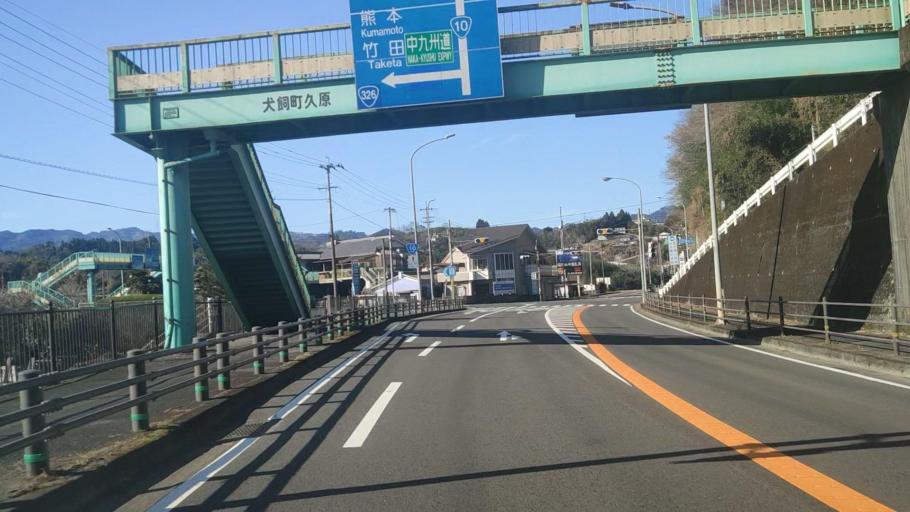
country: JP
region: Oita
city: Oita
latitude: 33.0716
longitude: 131.6388
